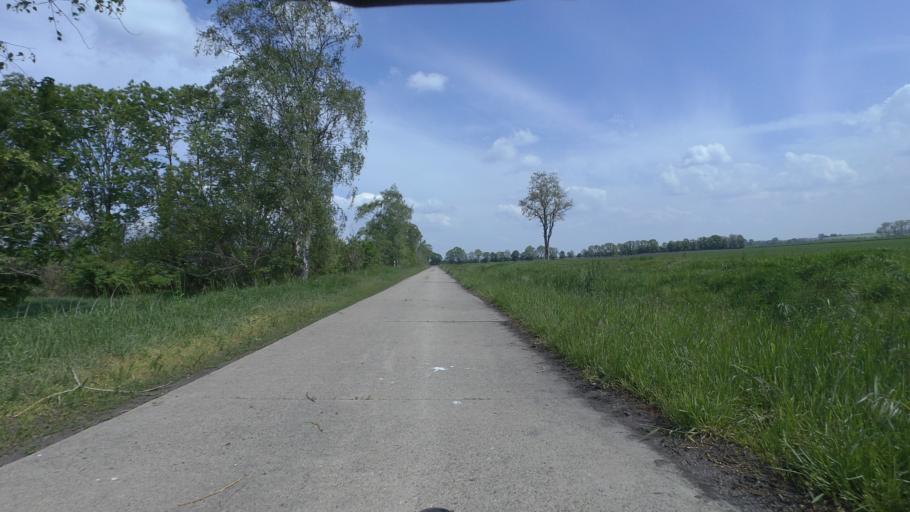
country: DE
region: Lower Saxony
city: Jerxheim
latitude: 52.0619
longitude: 10.9080
